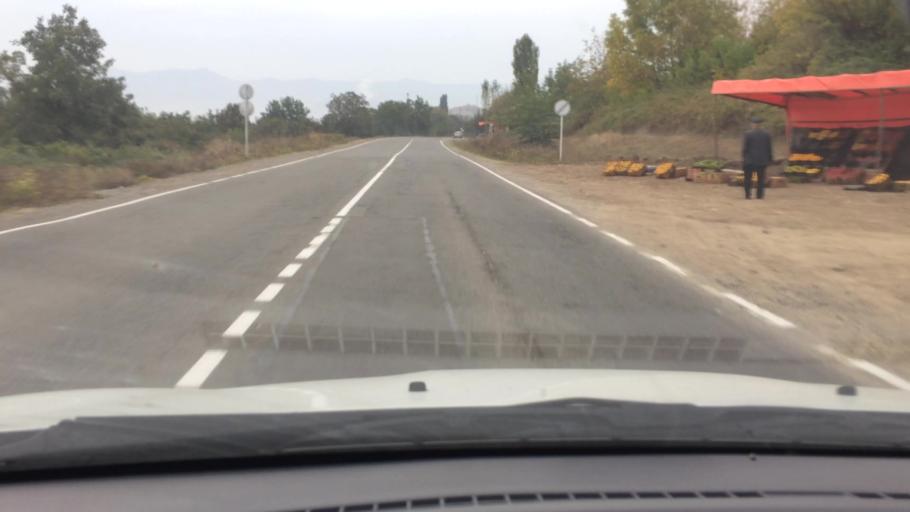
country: GE
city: Naghvarevi
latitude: 41.3031
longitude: 44.7897
